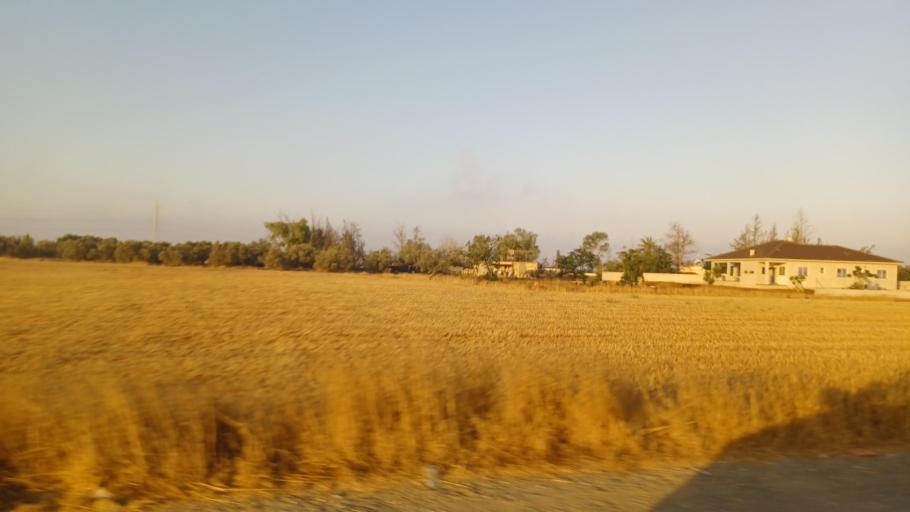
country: CY
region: Ammochostos
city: Avgorou
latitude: 35.0337
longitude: 33.8488
